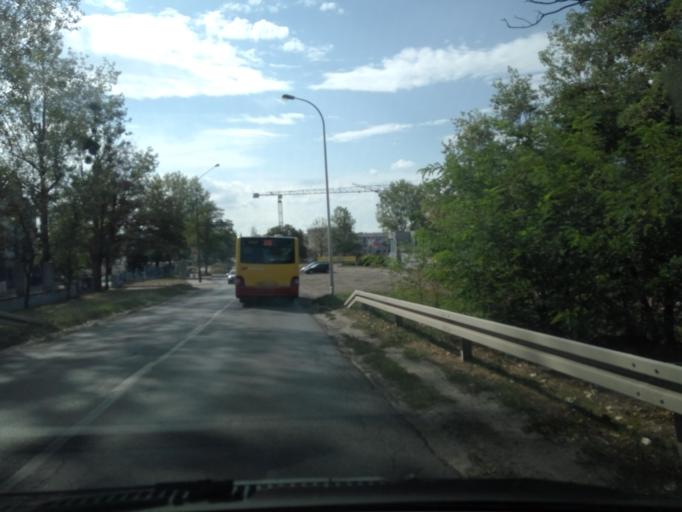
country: PL
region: Lower Silesian Voivodeship
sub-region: Powiat wroclawski
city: Wroclaw
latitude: 51.0783
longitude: 17.0714
